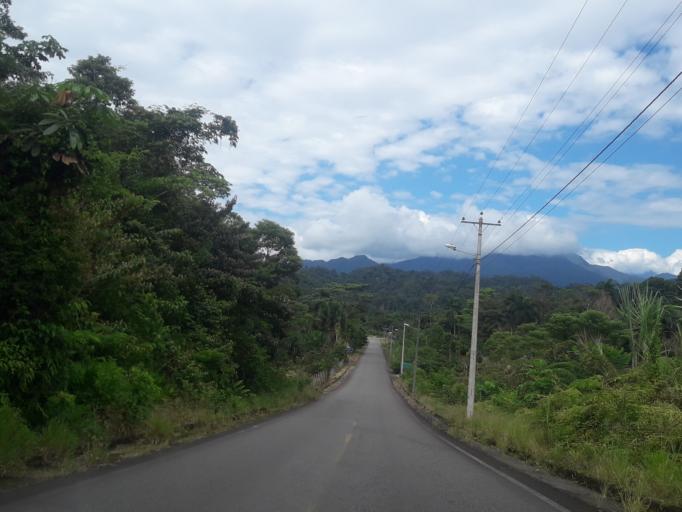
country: EC
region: Napo
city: Tena
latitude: -1.0599
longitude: -77.9006
